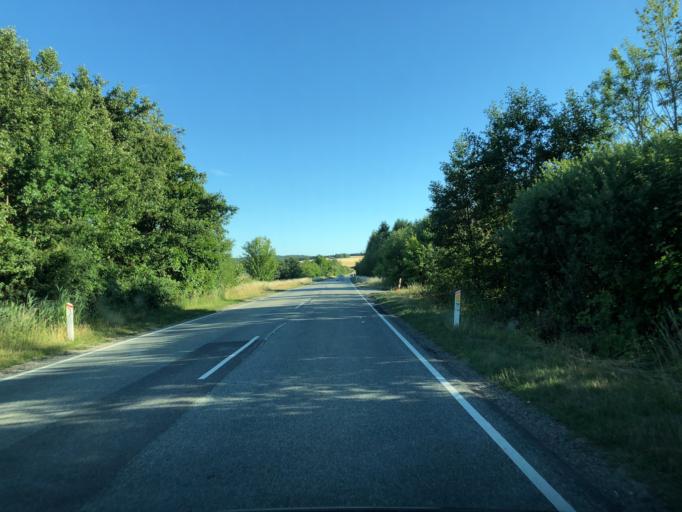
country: DK
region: Central Jutland
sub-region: Arhus Kommune
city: Framlev
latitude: 56.1332
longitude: 9.9975
